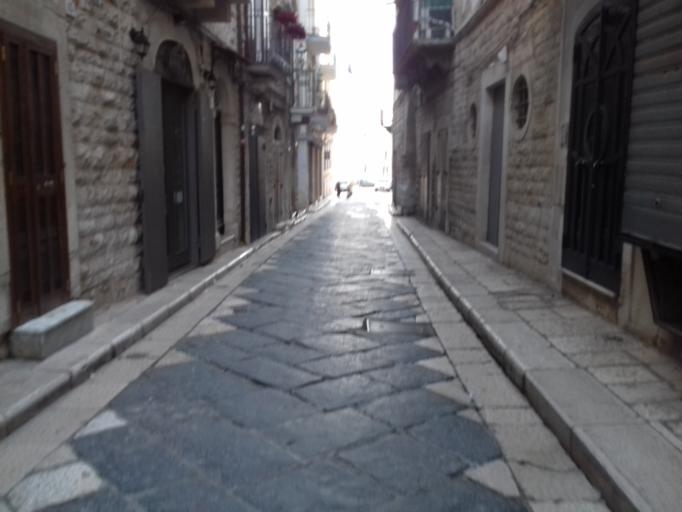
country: IT
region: Apulia
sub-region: Provincia di Bari
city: Ruvo di Puglia
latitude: 41.1152
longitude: 16.4859
